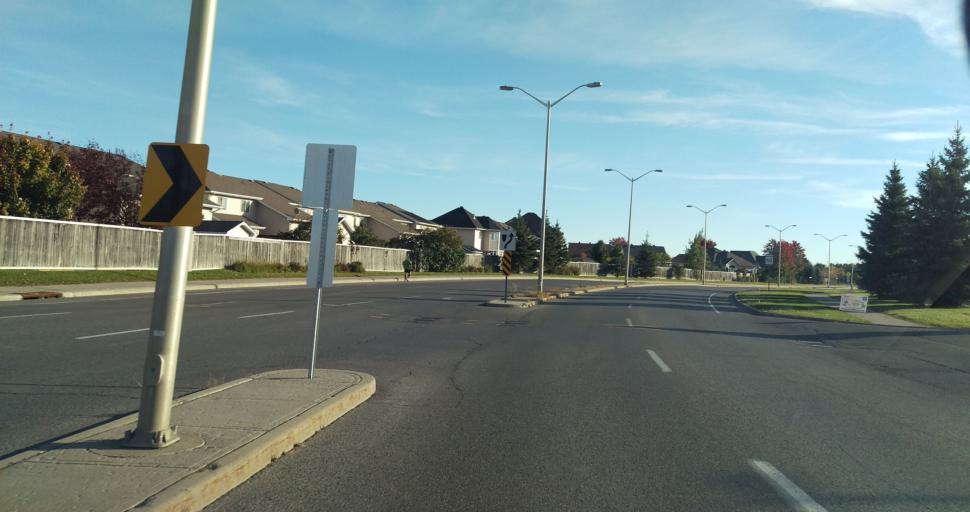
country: CA
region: Ontario
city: Clarence-Rockland
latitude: 45.4667
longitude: -75.4660
